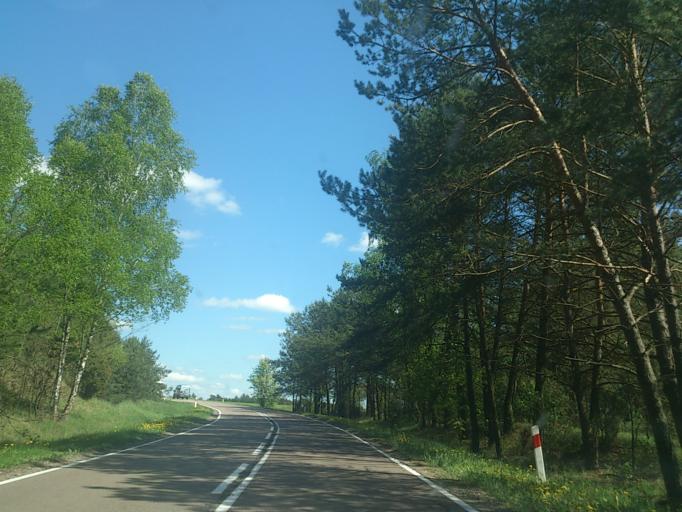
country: PL
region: Podlasie
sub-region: Powiat zambrowski
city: Rutki
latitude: 53.2040
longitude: 22.5418
